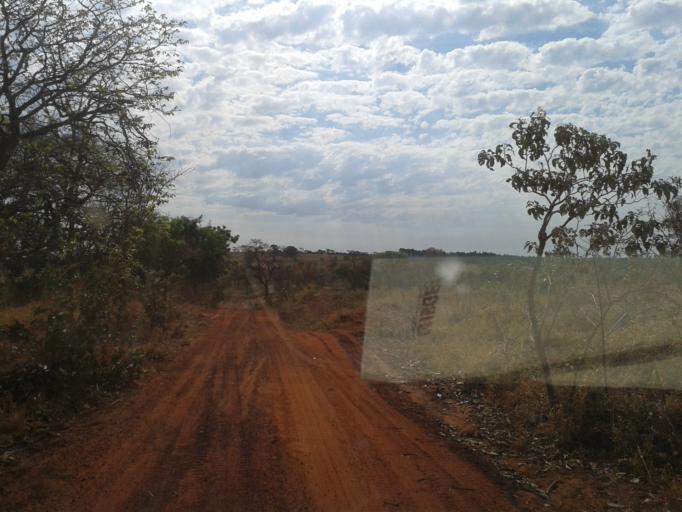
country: BR
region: Minas Gerais
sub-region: Ituiutaba
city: Ituiutaba
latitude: -19.0268
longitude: -49.2071
